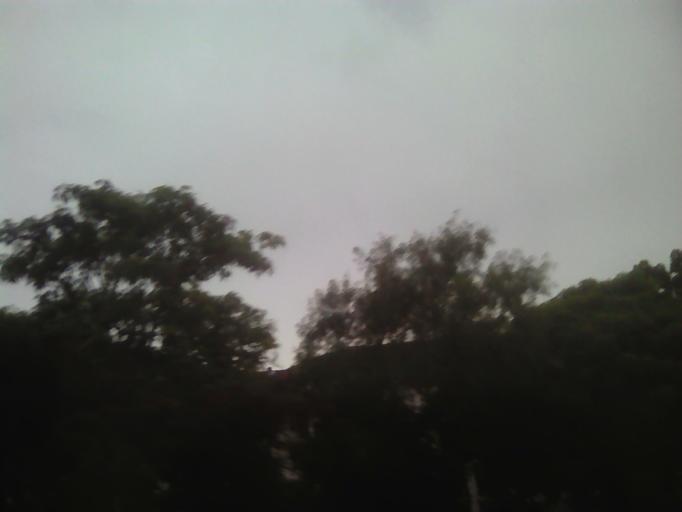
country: MY
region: Penang
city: Perai
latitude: 5.4025
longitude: 100.3963
